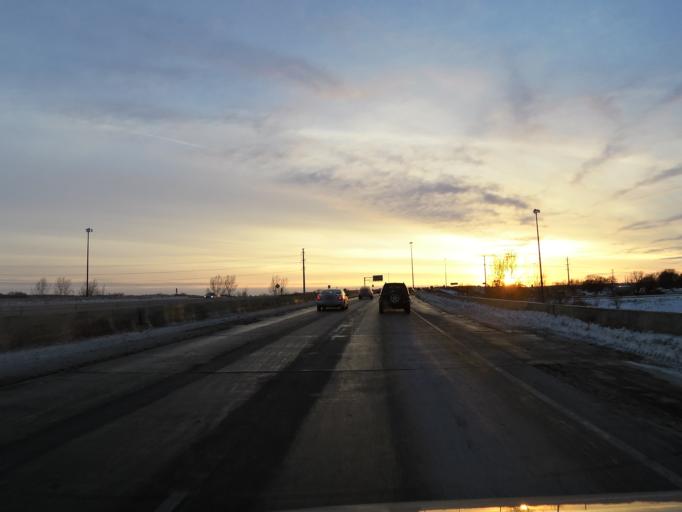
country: US
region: Minnesota
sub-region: Scott County
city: Savage
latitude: 44.7897
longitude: -93.4063
